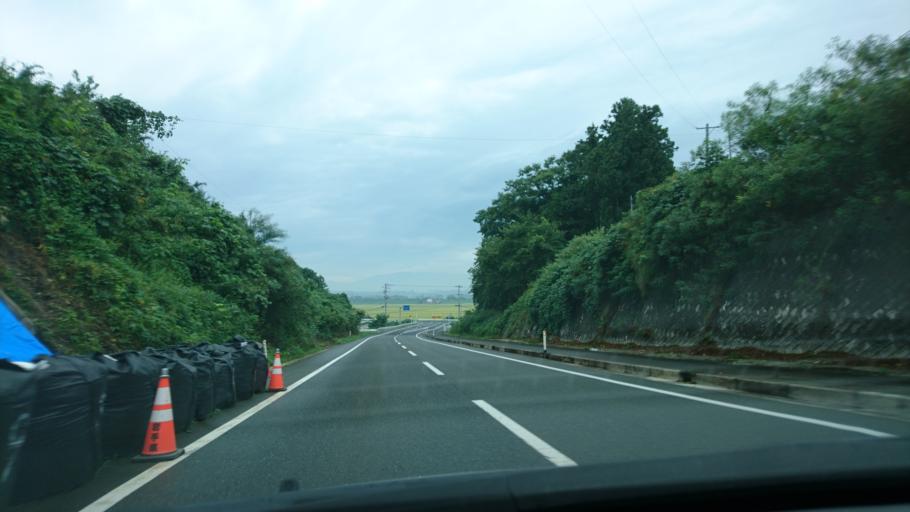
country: JP
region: Iwate
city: Mizusawa
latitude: 39.0549
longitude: 141.1753
